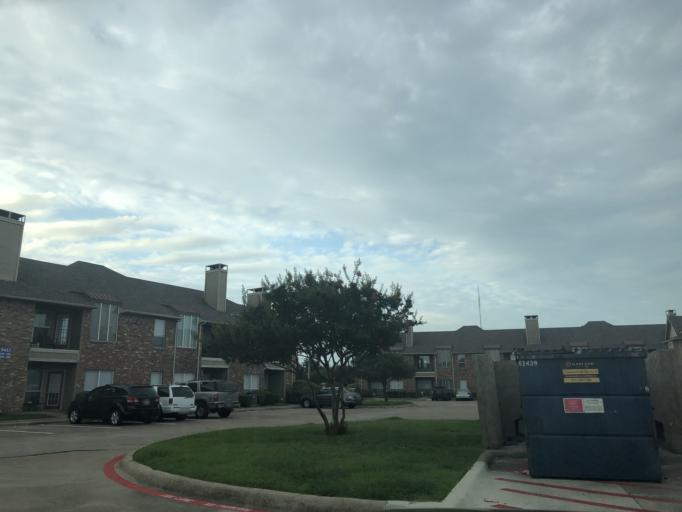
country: US
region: Texas
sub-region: Dallas County
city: Sunnyvale
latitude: 32.8496
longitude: -96.5641
